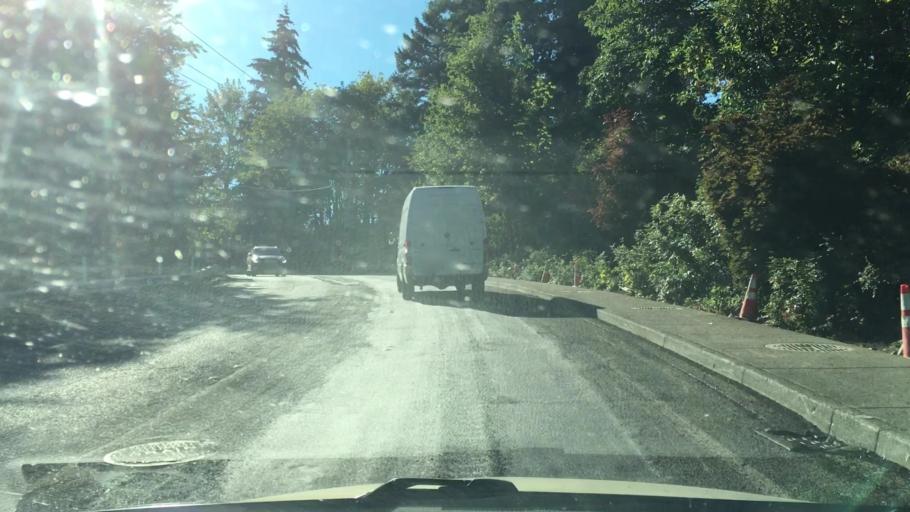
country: US
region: Washington
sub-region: King County
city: Eastgate
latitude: 47.5789
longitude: -122.1264
